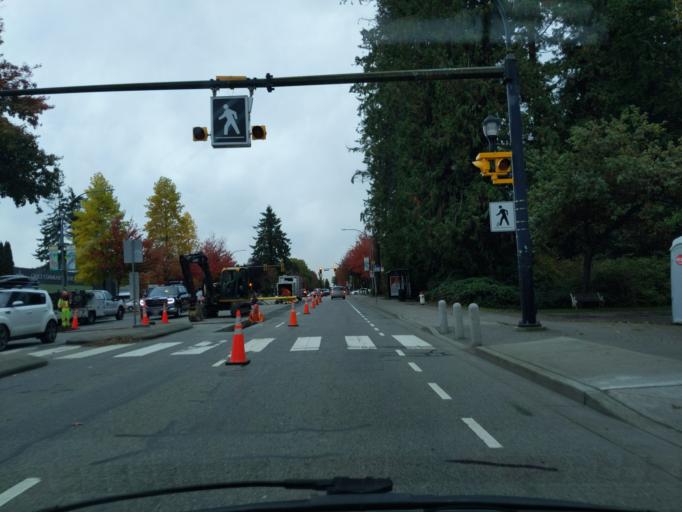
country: CA
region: British Columbia
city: Pitt Meadows
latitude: 49.2257
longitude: -122.6897
